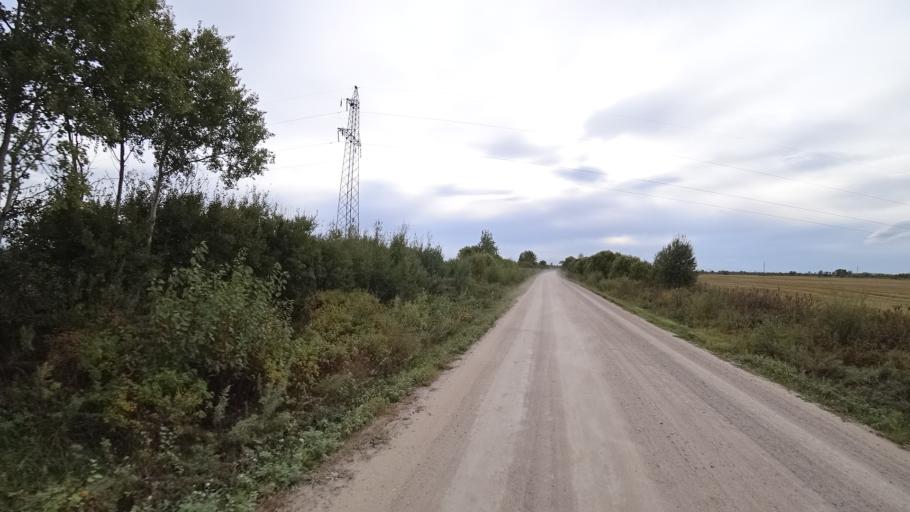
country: RU
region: Amur
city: Arkhara
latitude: 49.3739
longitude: 130.1498
